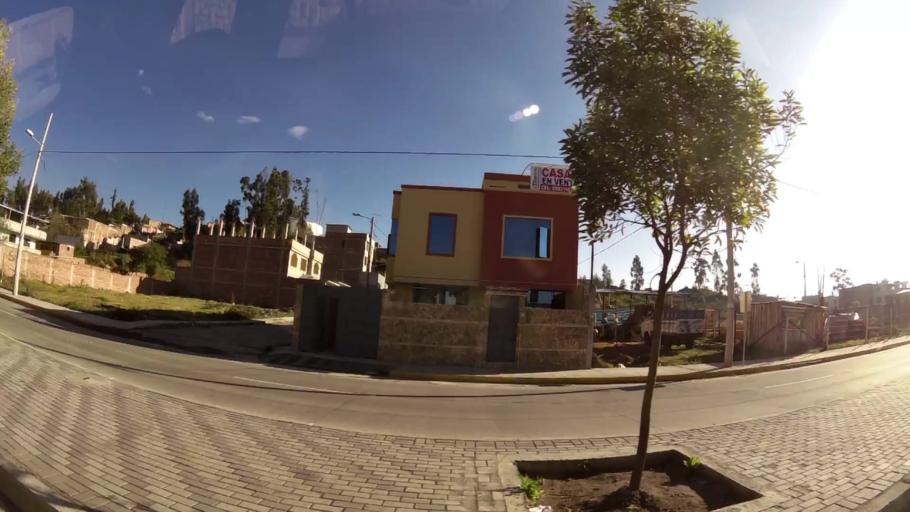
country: EC
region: Chimborazo
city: Riobamba
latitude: -1.6738
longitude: -78.6327
